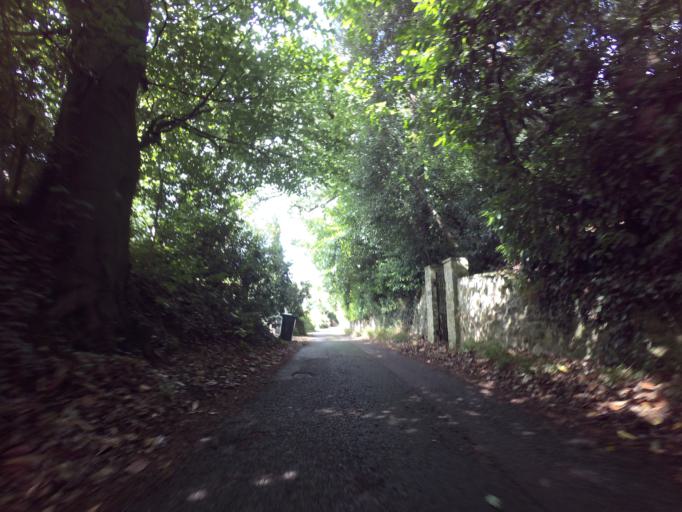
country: GB
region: England
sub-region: Kent
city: Borough Green
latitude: 51.2834
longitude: 0.2740
